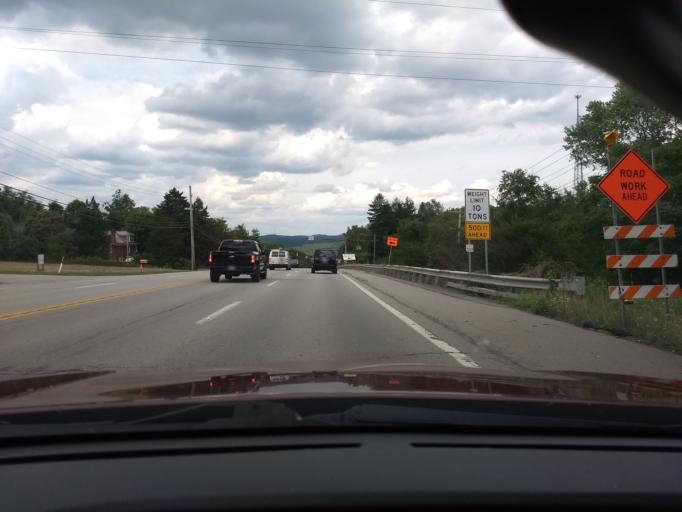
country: US
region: Pennsylvania
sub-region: Armstrong County
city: Freeport
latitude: 40.6636
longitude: -79.7052
